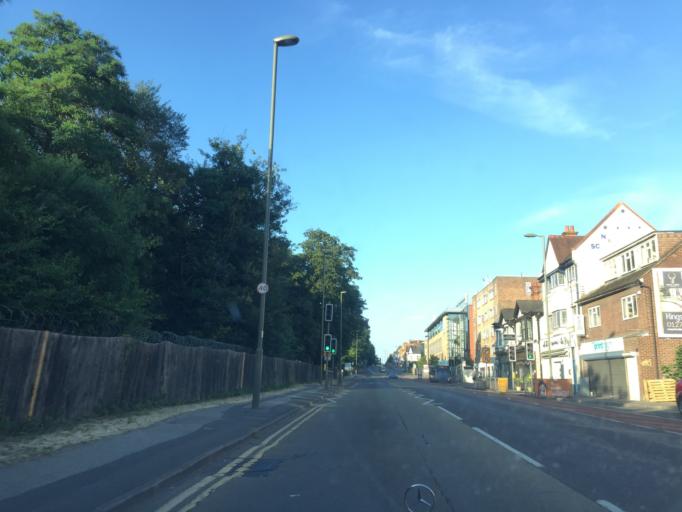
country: GB
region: England
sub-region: Surrey
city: Camberley
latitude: 51.3352
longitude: -0.7642
